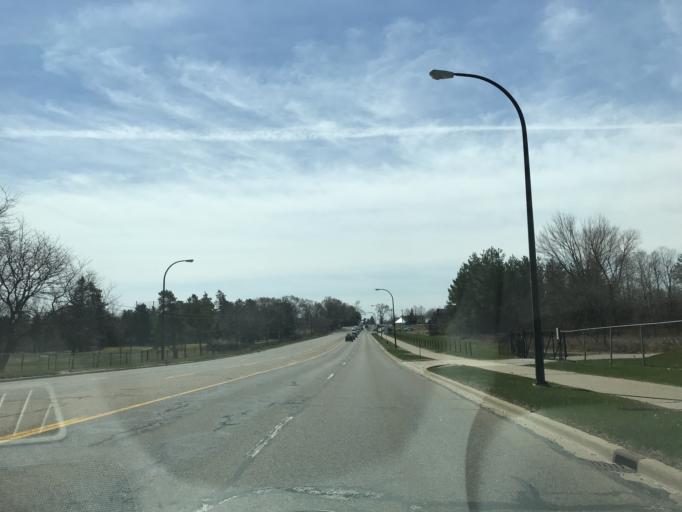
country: US
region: Michigan
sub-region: Washtenaw County
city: Ann Arbor
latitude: 42.2595
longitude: -83.7502
